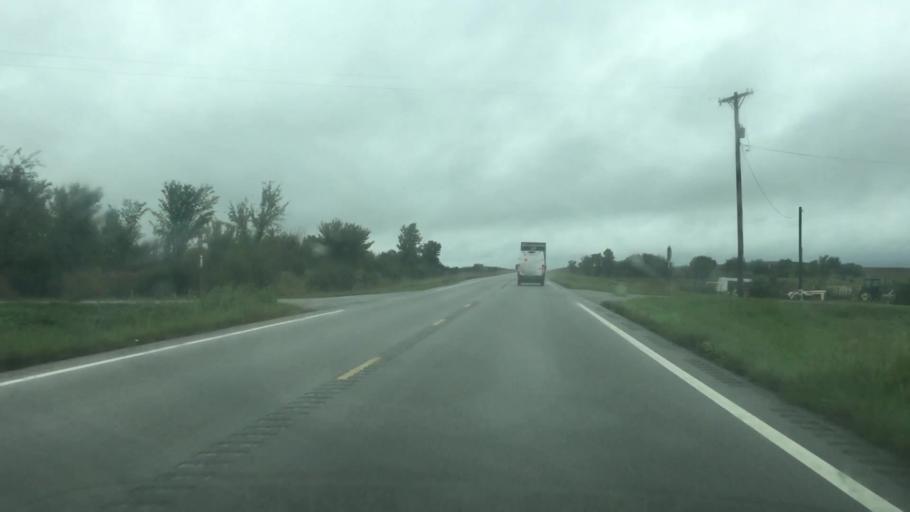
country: US
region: Kansas
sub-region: Allen County
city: Iola
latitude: 38.0970
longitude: -95.3587
